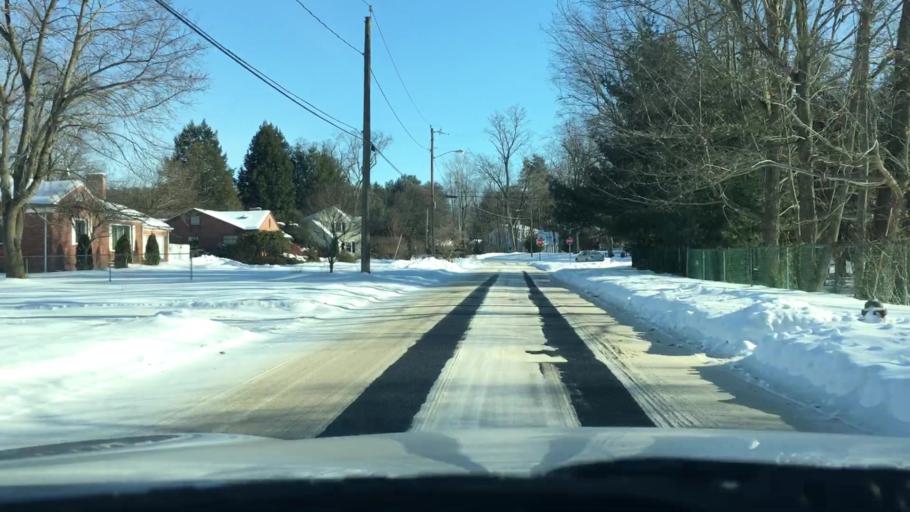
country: US
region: Massachusetts
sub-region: Hampden County
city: Longmeadow
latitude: 42.0495
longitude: -72.5752
